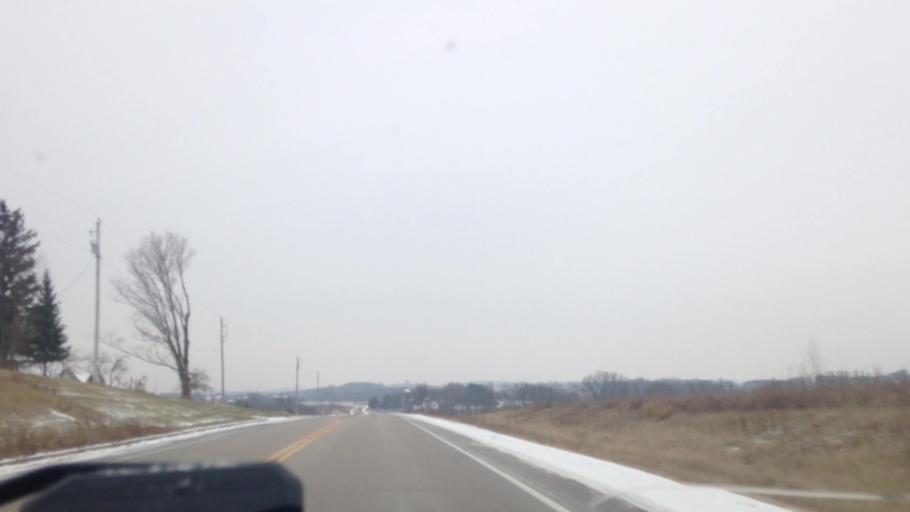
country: US
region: Wisconsin
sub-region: Dodge County
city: Hustisford
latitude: 43.3833
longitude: -88.5419
